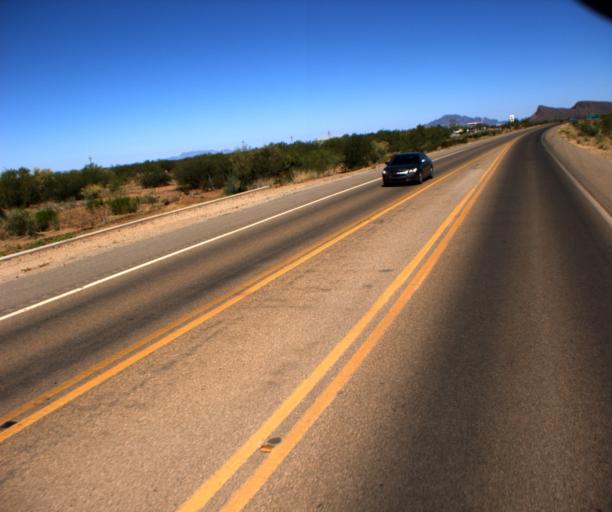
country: US
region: Arizona
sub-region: Pima County
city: Sells
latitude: 31.9230
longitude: -111.8946
